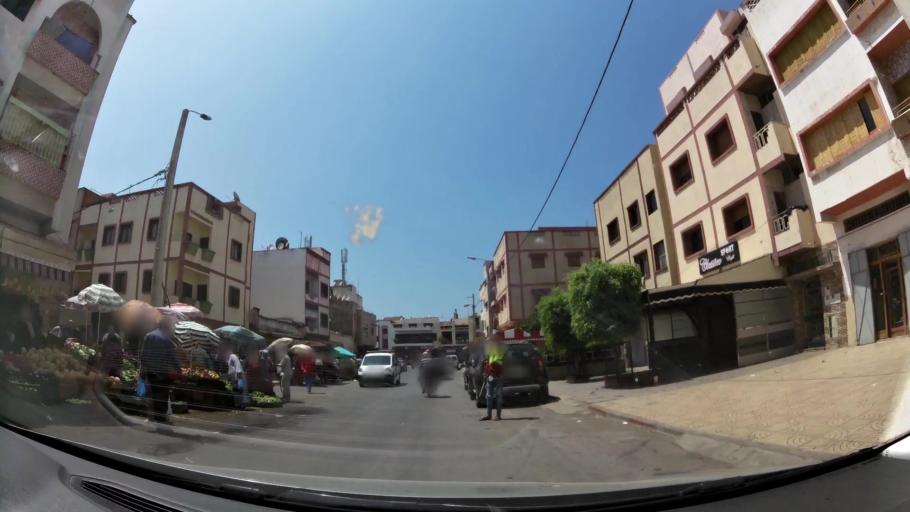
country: MA
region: Rabat-Sale-Zemmour-Zaer
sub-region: Skhirate-Temara
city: Temara
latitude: 33.9720
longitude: -6.8917
